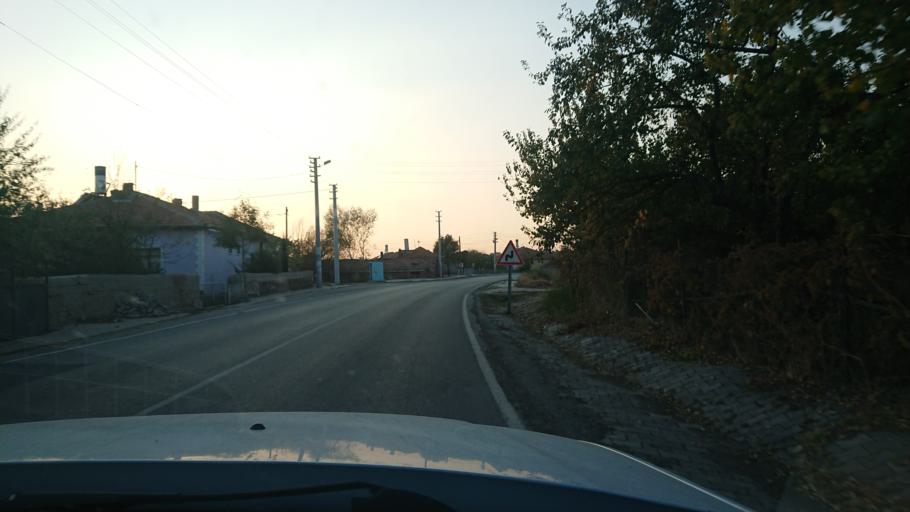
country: TR
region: Aksaray
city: Aksaray
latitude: 38.2993
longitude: 34.0742
